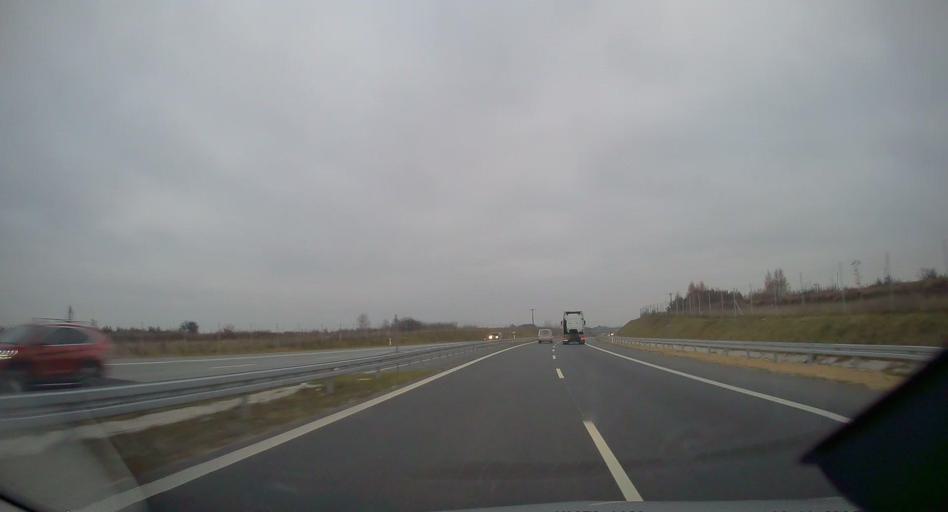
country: PL
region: Silesian Voivodeship
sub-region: Powiat bedzinski
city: Mierzecice
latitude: 50.4425
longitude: 19.1437
